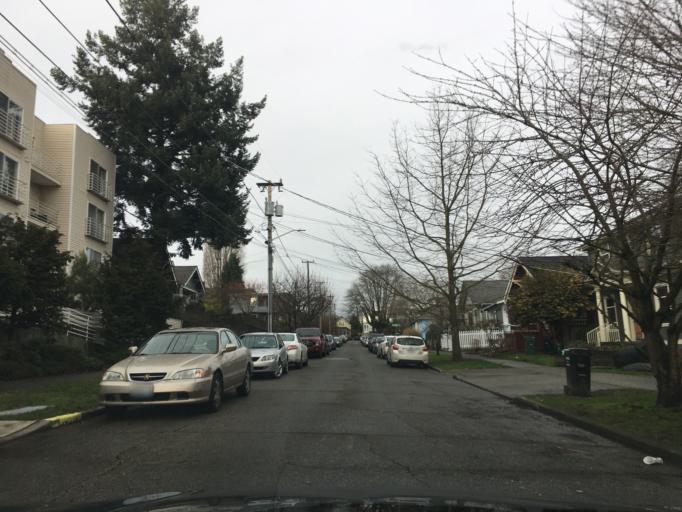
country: US
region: Washington
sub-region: King County
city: Seattle
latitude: 47.6595
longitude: -122.3511
